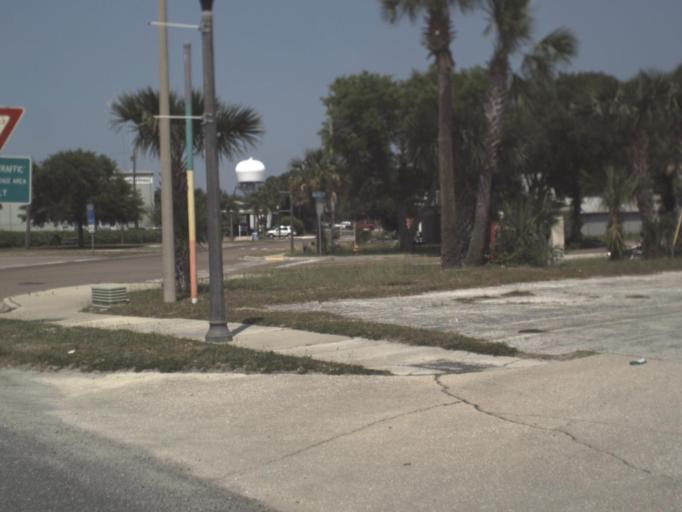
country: US
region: Florida
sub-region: Duval County
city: Atlantic Beach
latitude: 30.3949
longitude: -81.4296
